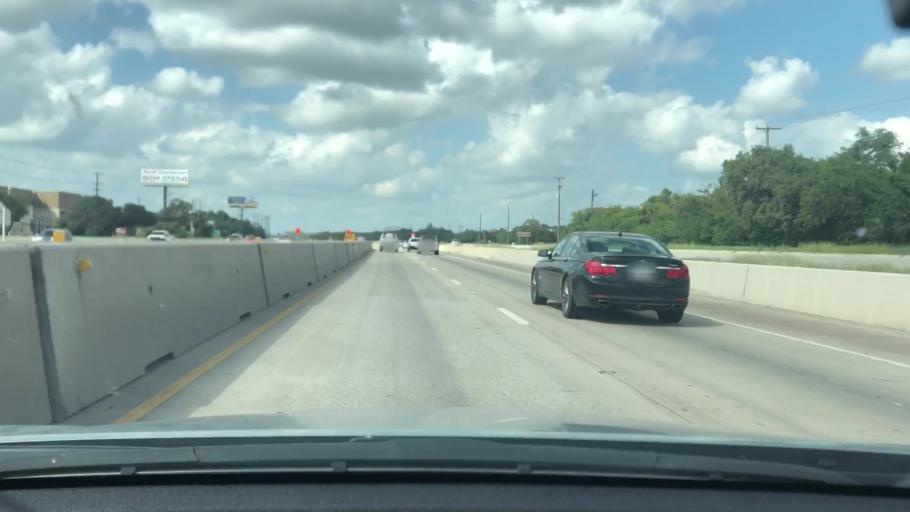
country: US
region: Texas
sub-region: Bexar County
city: Cross Mountain
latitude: 29.6314
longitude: -98.6138
